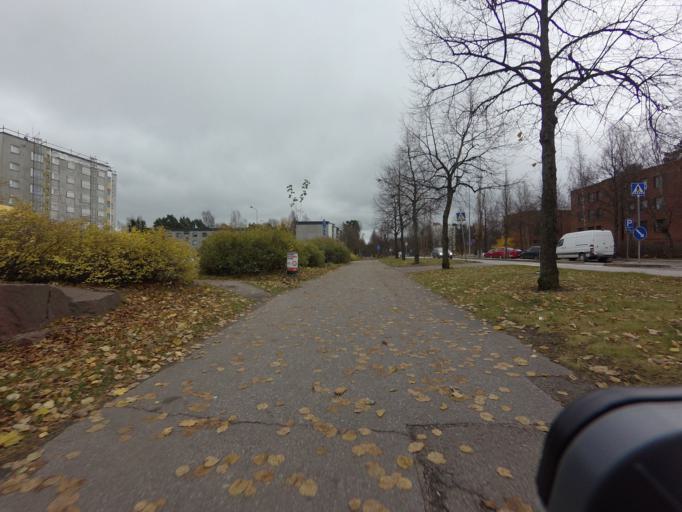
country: FI
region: Uusimaa
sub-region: Helsinki
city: Koukkuniemi
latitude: 60.1579
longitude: 24.7432
